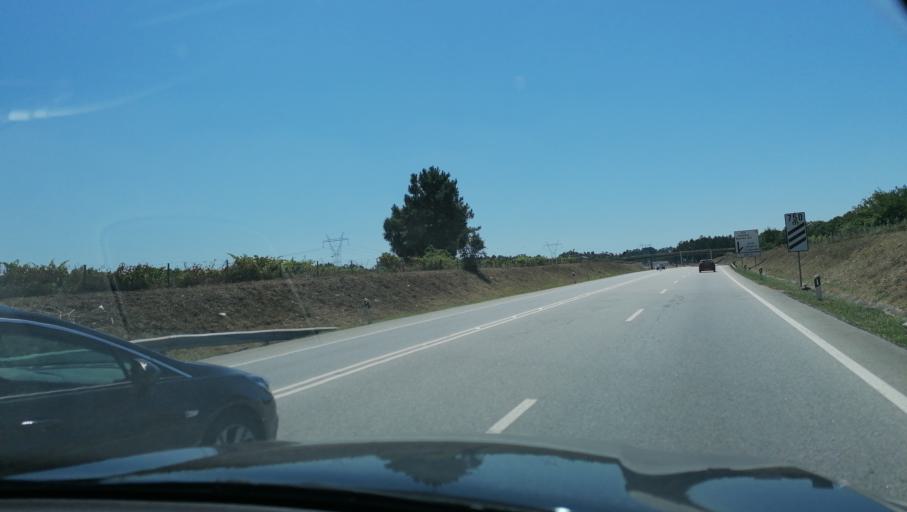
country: PT
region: Aveiro
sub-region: Agueda
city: Agueda
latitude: 40.5621
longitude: -8.4757
